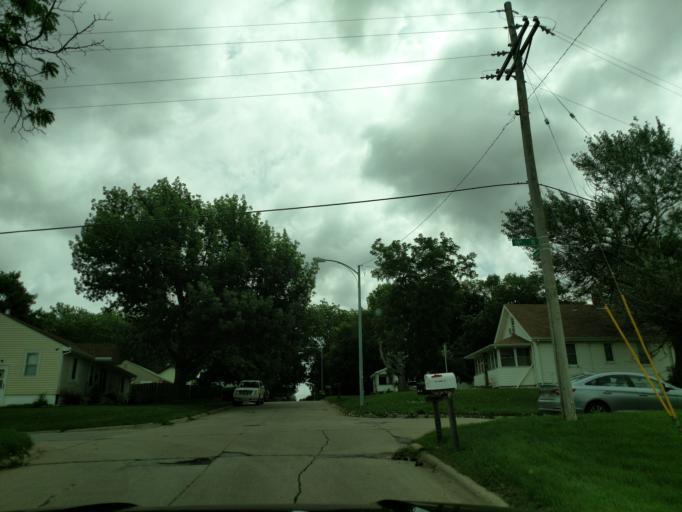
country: US
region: Nebraska
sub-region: Sarpy County
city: La Vista
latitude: 41.2092
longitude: -96.0027
